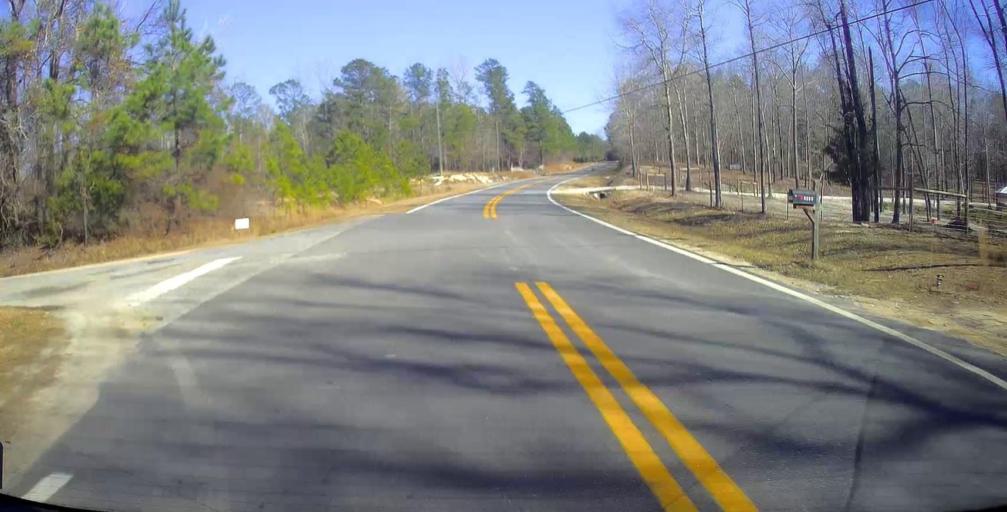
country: US
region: Georgia
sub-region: Peach County
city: Fort Valley
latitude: 32.6422
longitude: -83.9117
